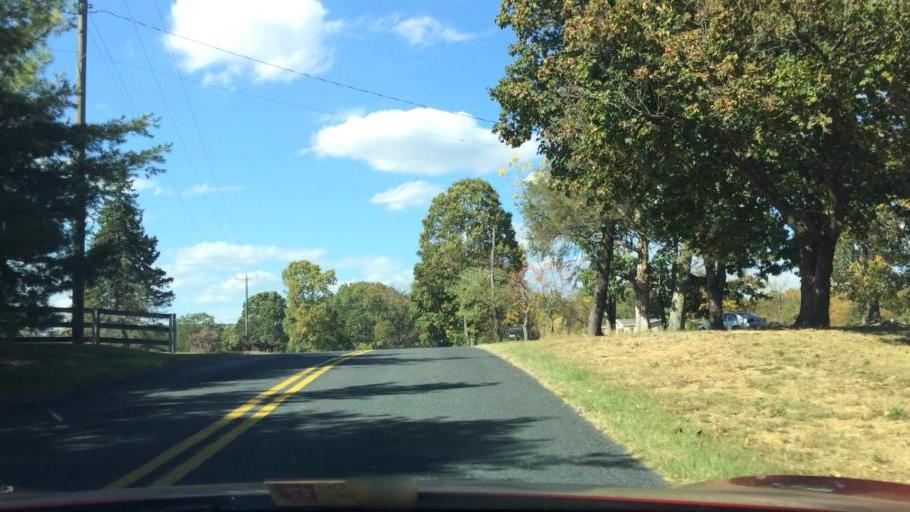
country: US
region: Virginia
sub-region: Frederick County
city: Shawnee Land
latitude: 39.3294
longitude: -78.3200
